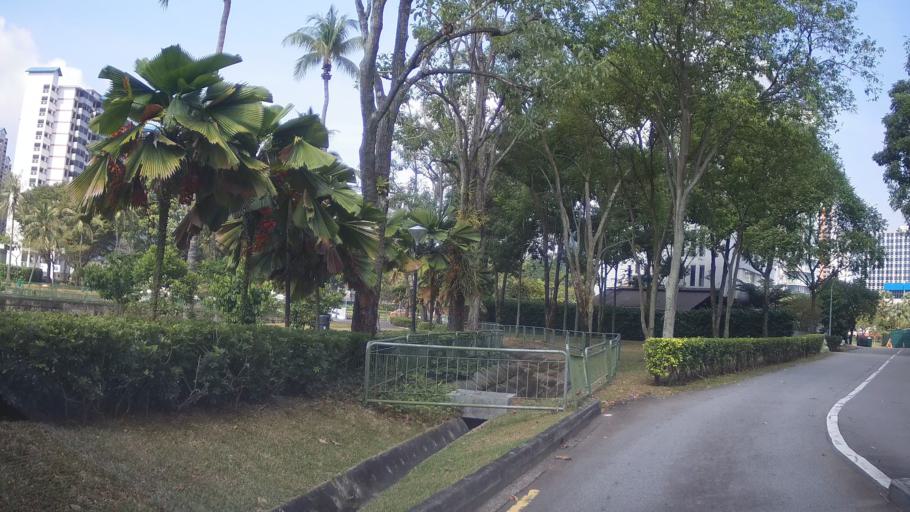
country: SG
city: Singapore
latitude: 1.3059
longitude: 103.8669
